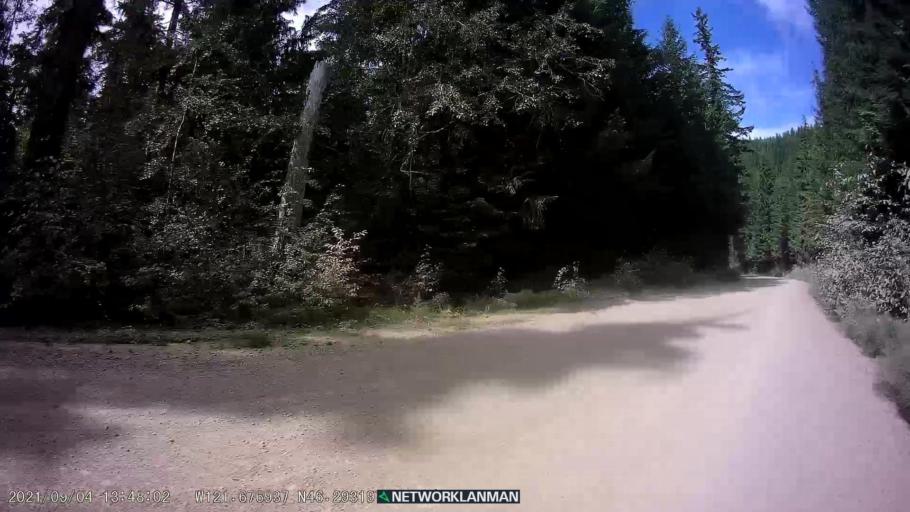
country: US
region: Washington
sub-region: Skamania County
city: Carson
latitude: 46.2934
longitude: -121.6768
